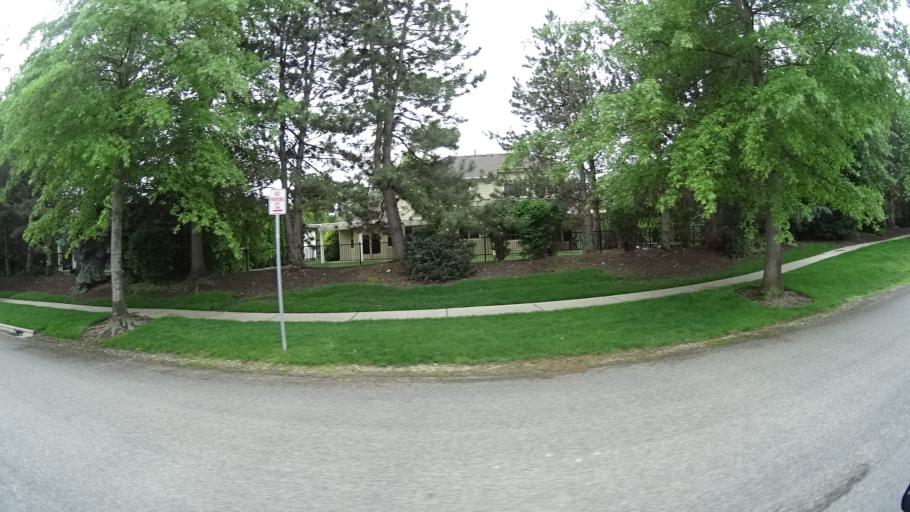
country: US
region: Idaho
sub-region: Ada County
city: Eagle
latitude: 43.6861
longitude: -116.3606
